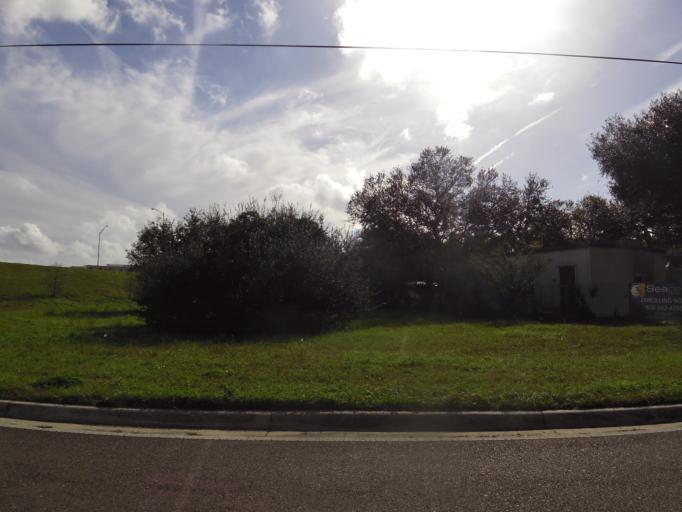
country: US
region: Florida
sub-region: Duval County
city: Jacksonville
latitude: 30.3292
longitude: -81.5560
